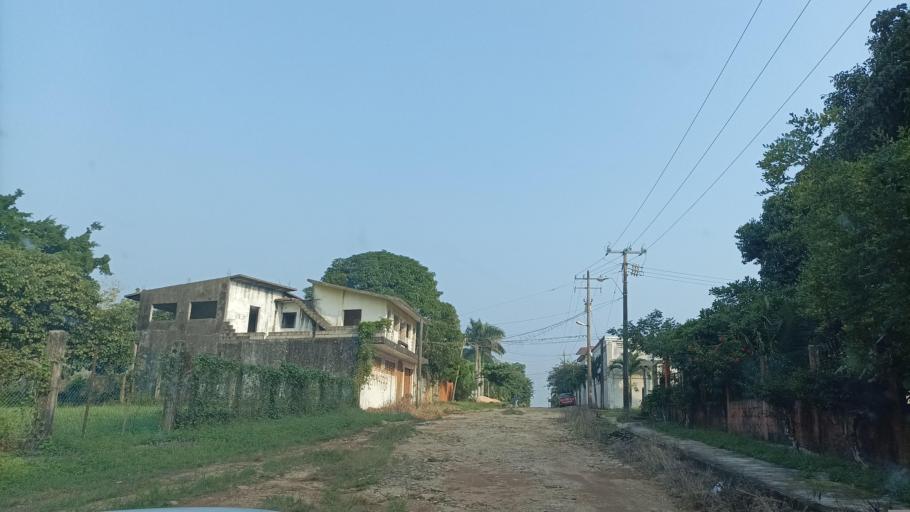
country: MX
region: Veracruz
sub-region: Cosoleacaque
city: Residencial las Olas
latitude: 18.1003
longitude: -94.5703
